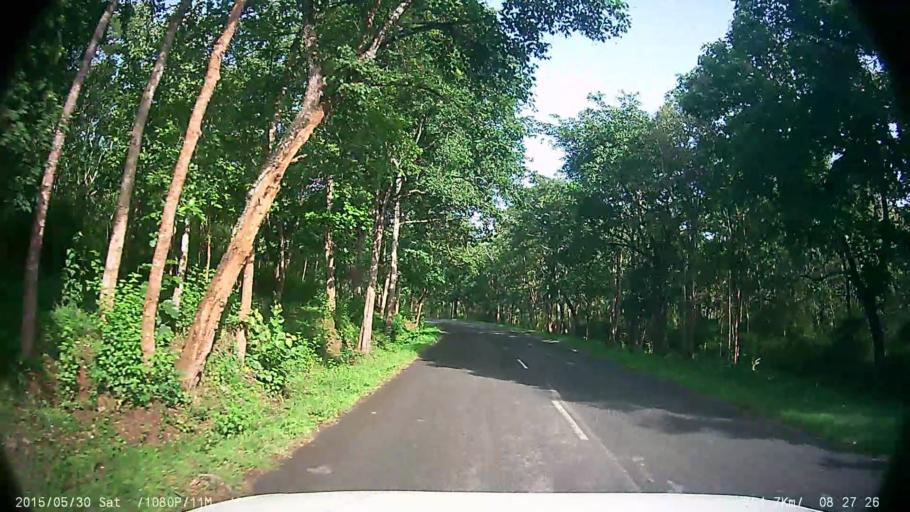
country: IN
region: Karnataka
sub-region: Chamrajnagar
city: Gundlupet
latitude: 11.7482
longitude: 76.4908
